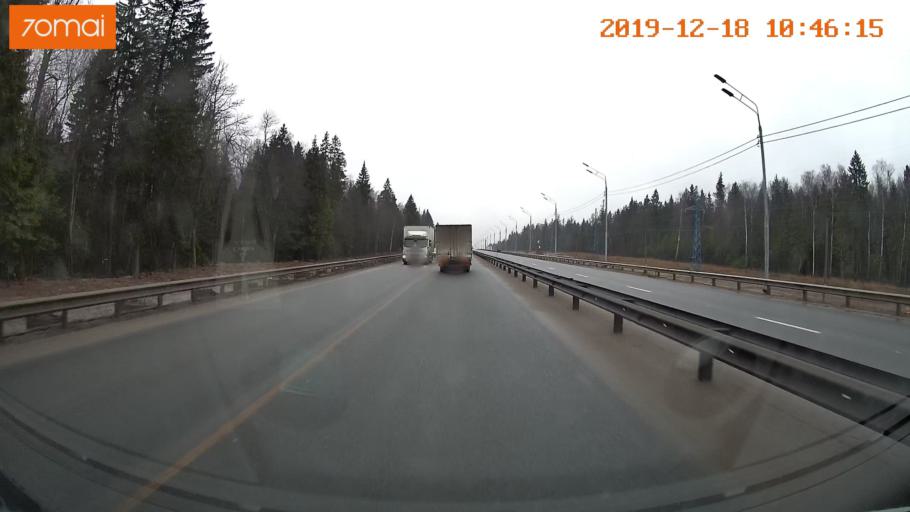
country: RU
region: Moskovskaya
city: Aprelevka
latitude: 55.4829
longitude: 37.0505
